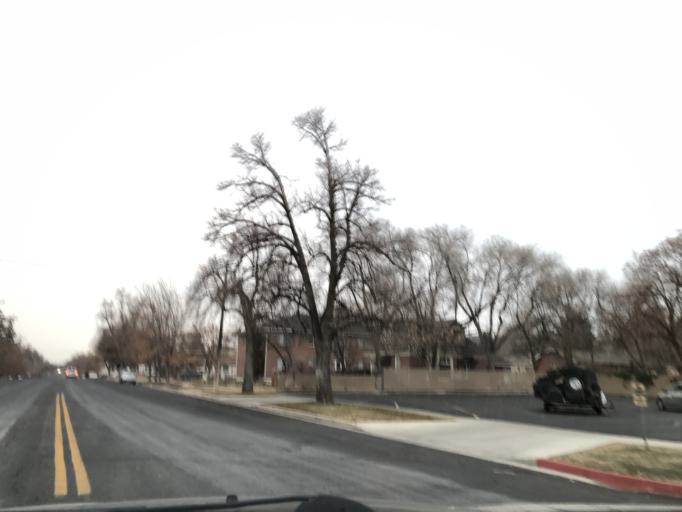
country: US
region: Utah
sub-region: Cache County
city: Logan
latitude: 41.7370
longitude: -111.8220
